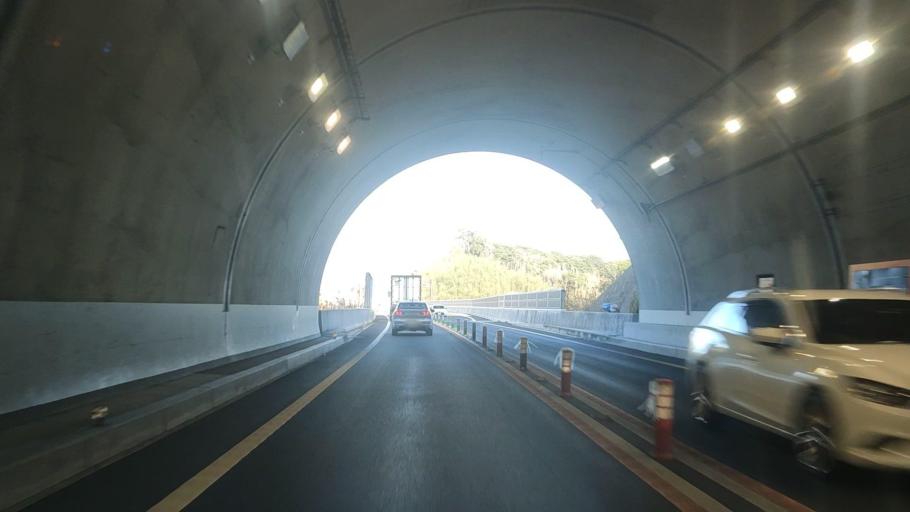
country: JP
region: Fukuoka
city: Kanda
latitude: 33.7905
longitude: 130.9697
